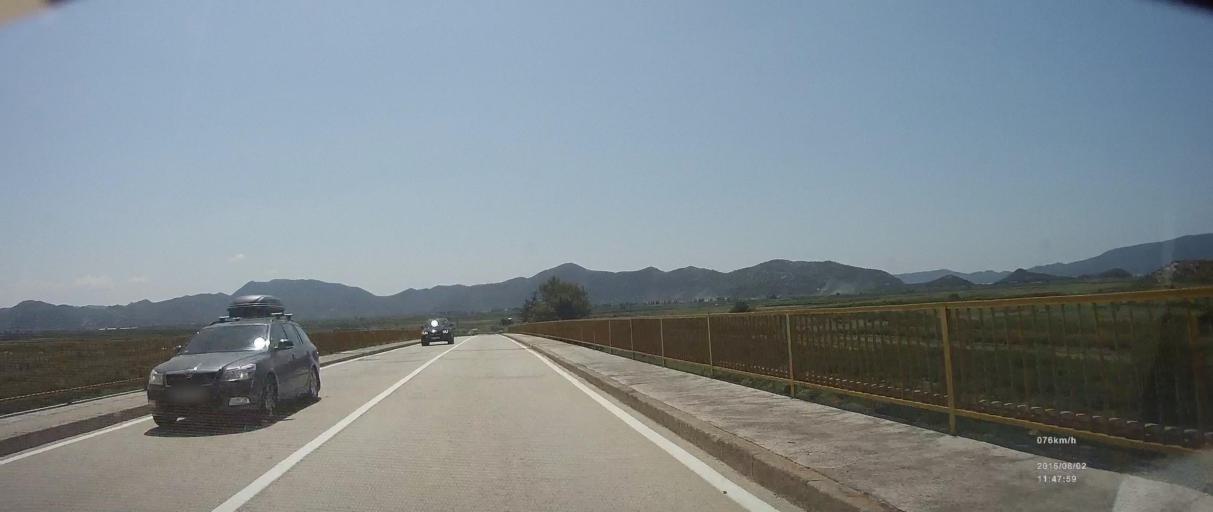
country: HR
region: Dubrovacko-Neretvanska
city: Komin
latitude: 43.0380
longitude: 17.4852
